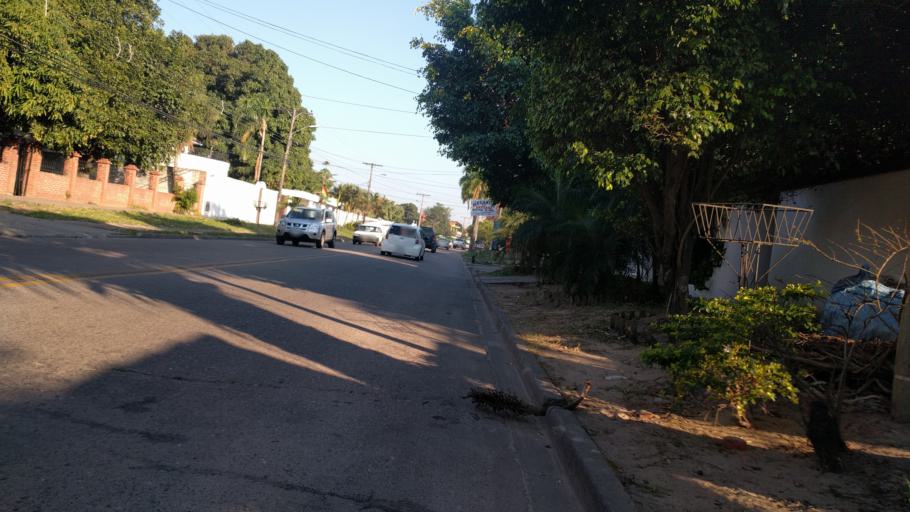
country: BO
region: Santa Cruz
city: Santa Cruz de la Sierra
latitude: -17.8107
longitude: -63.1668
